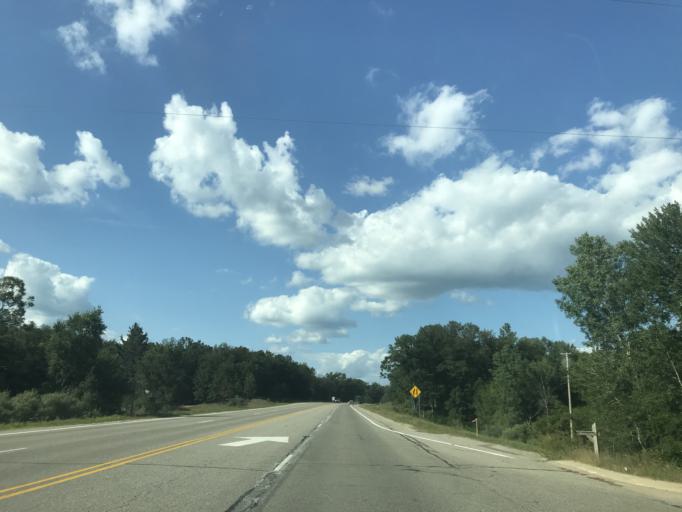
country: US
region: Michigan
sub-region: Newaygo County
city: Newaygo
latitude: 43.4305
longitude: -85.7952
